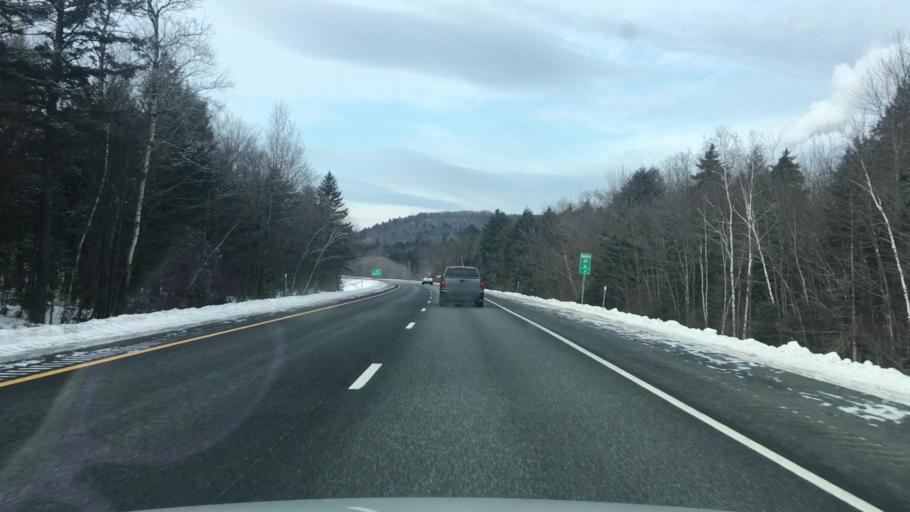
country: US
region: New Hampshire
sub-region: Sullivan County
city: Springfield
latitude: 43.4393
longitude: -72.0521
